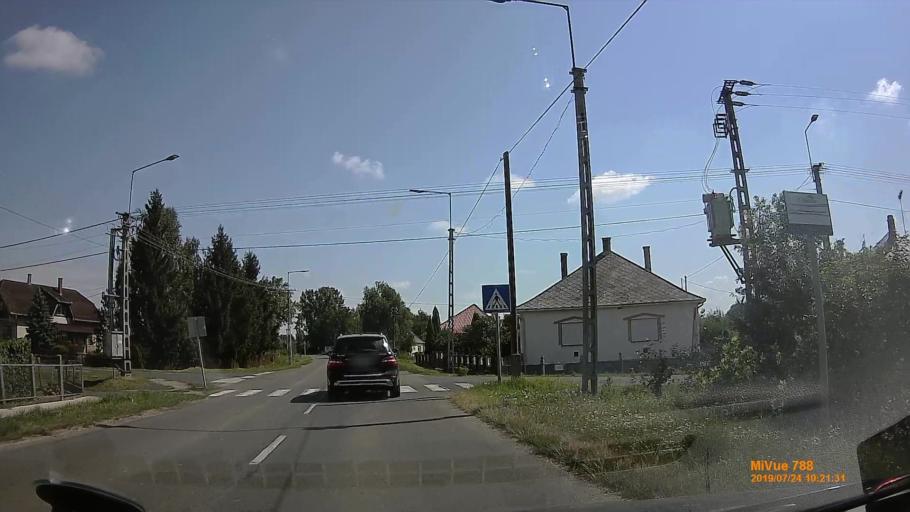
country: HU
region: Szabolcs-Szatmar-Bereg
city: Vasarosnameny
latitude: 48.1273
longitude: 22.3471
